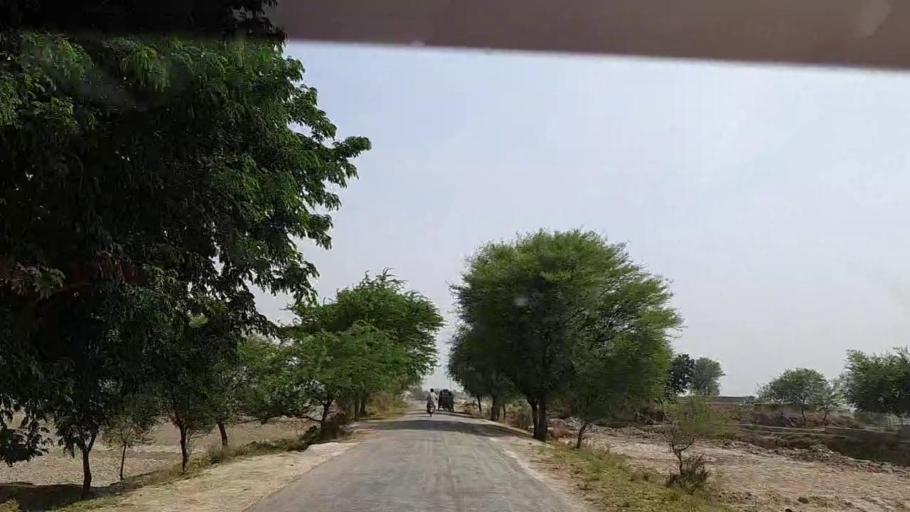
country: PK
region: Sindh
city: Khairpur Nathan Shah
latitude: 27.0714
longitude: 67.6879
